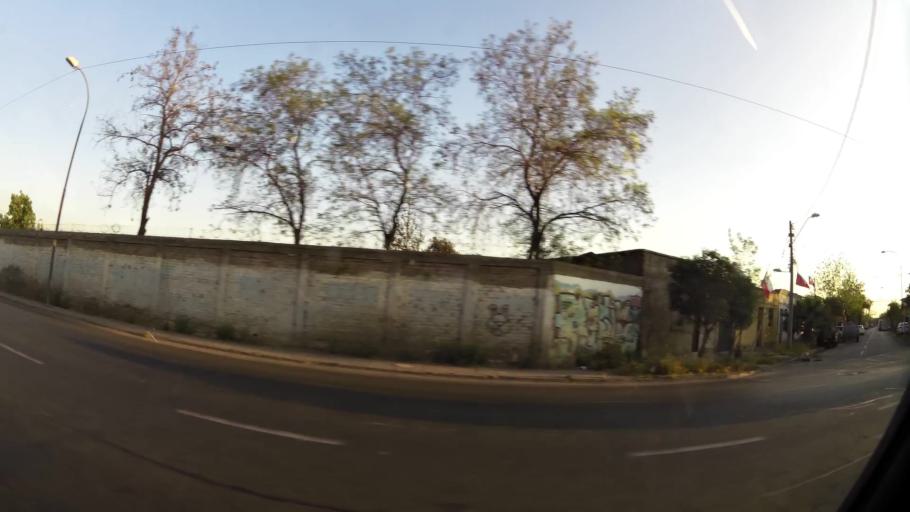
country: CL
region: Santiago Metropolitan
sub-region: Provincia de Santiago
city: Santiago
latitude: -33.4783
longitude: -70.6881
